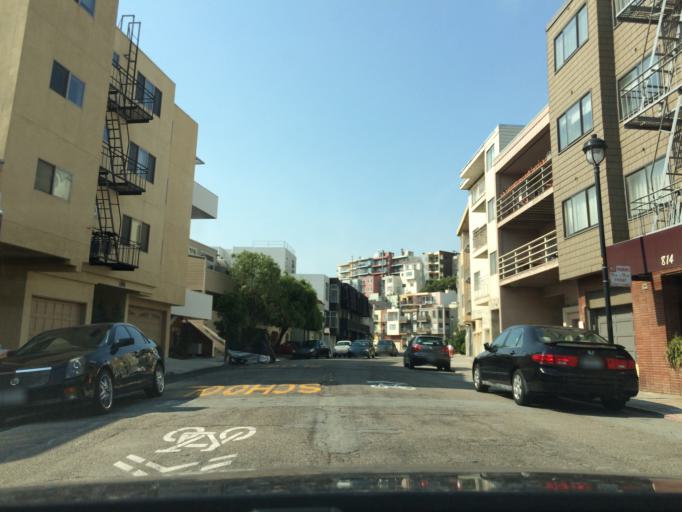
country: US
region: California
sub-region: San Francisco County
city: San Francisco
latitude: 37.7538
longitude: -122.4431
